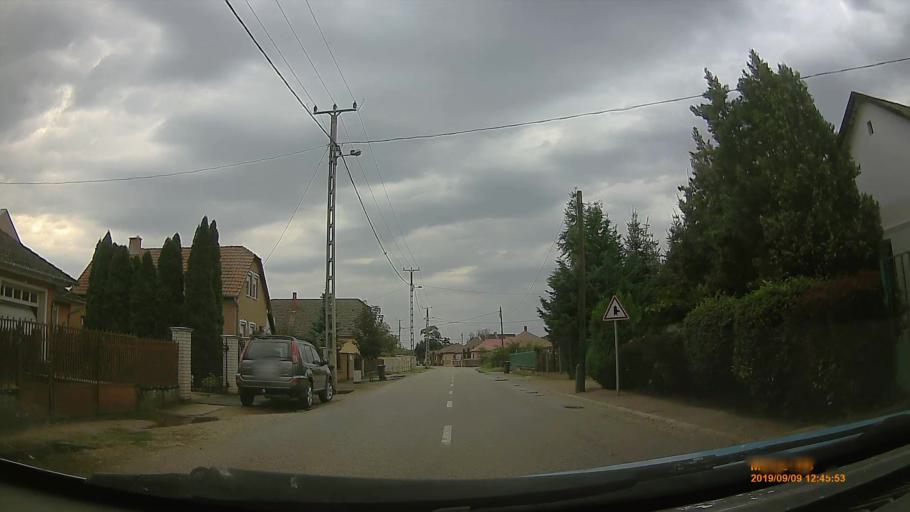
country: HU
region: Szabolcs-Szatmar-Bereg
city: Nyirpazony
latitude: 47.9521
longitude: 21.8051
